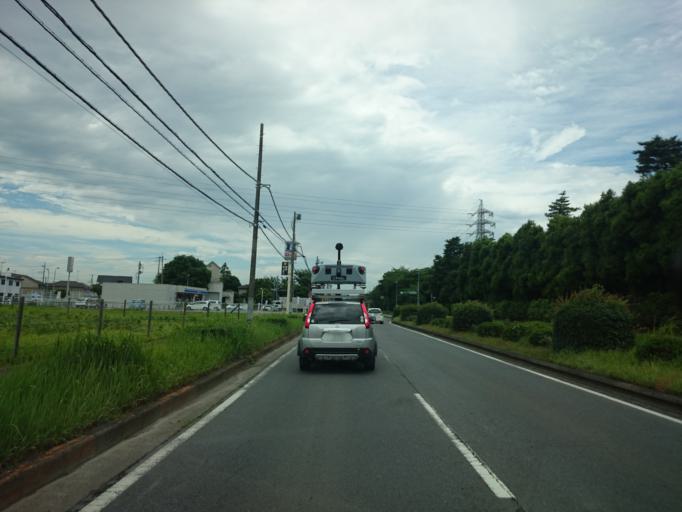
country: JP
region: Ibaraki
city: Tsukuba
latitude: 36.1326
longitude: 140.0783
